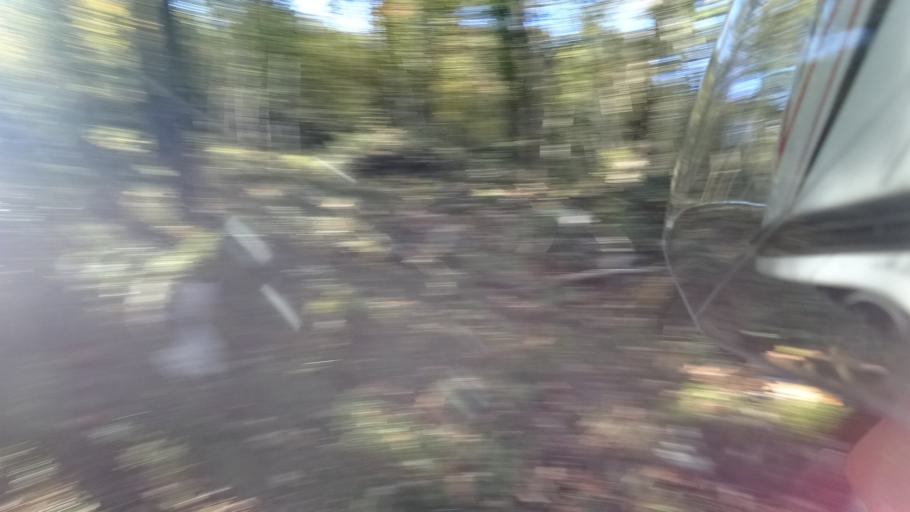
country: HR
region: Primorsko-Goranska
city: Matulji
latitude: 45.3889
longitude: 14.2910
